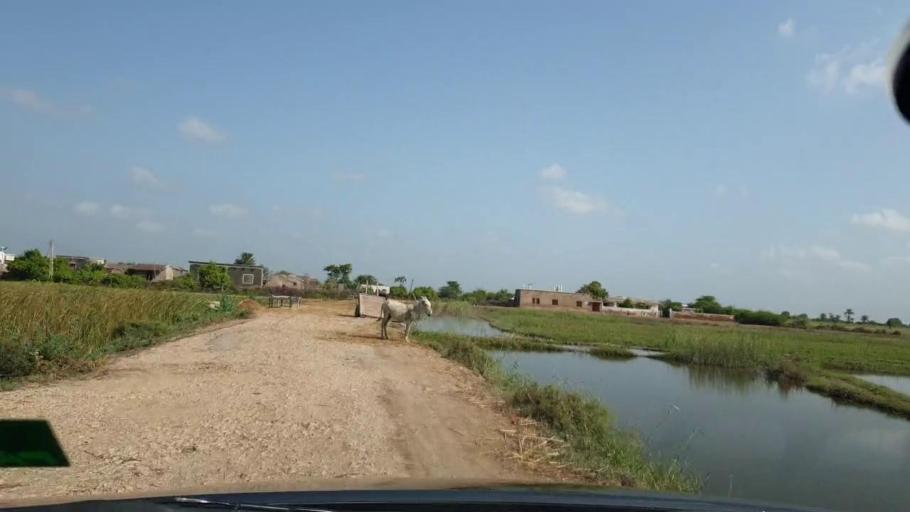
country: PK
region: Sindh
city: Tando Bago
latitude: 24.6464
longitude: 69.0940
